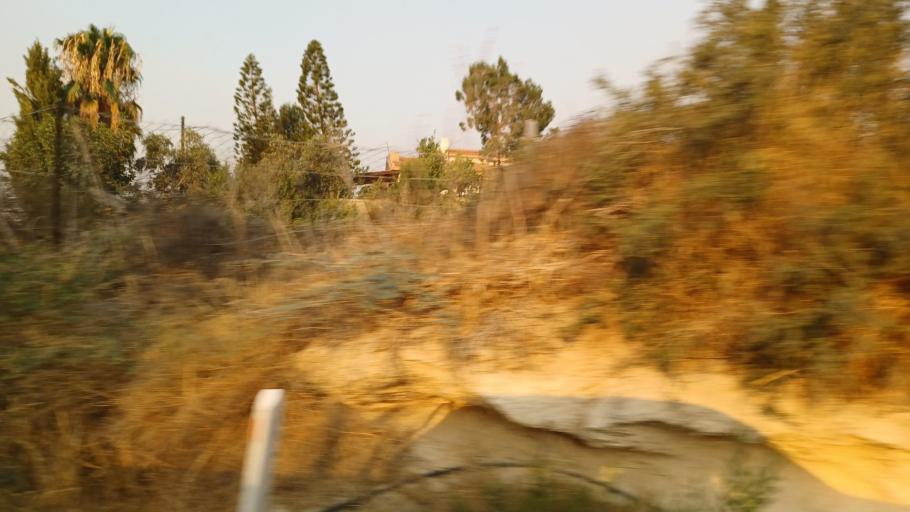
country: CY
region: Limassol
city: Pissouri
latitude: 34.6783
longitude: 32.6958
